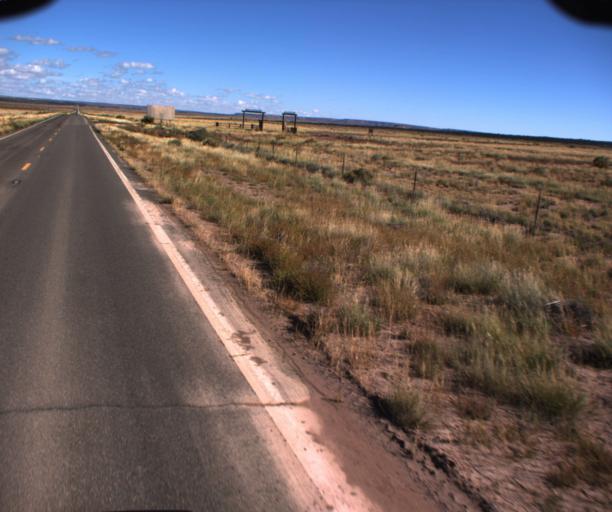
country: US
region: Arizona
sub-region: Apache County
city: Saint Johns
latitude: 34.6735
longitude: -109.2864
